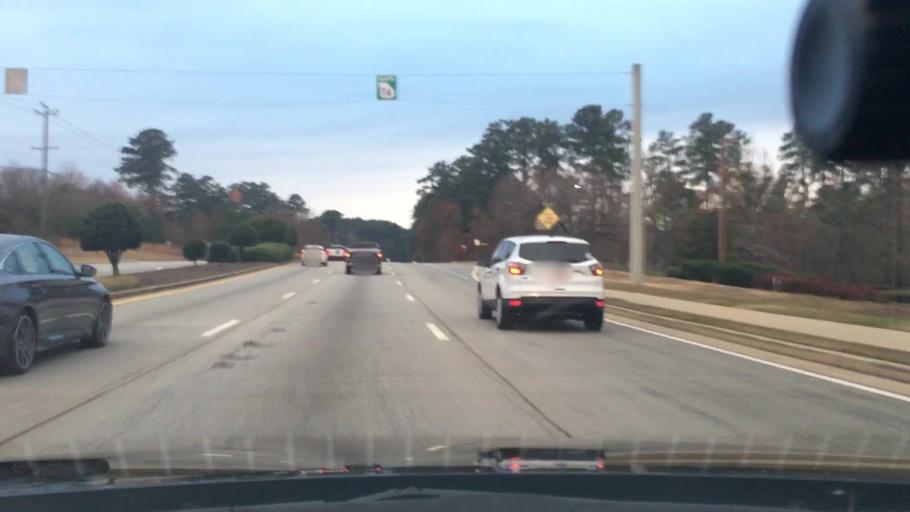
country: US
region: Georgia
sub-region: Fayette County
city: Peachtree City
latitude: 33.3981
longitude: -84.5920
